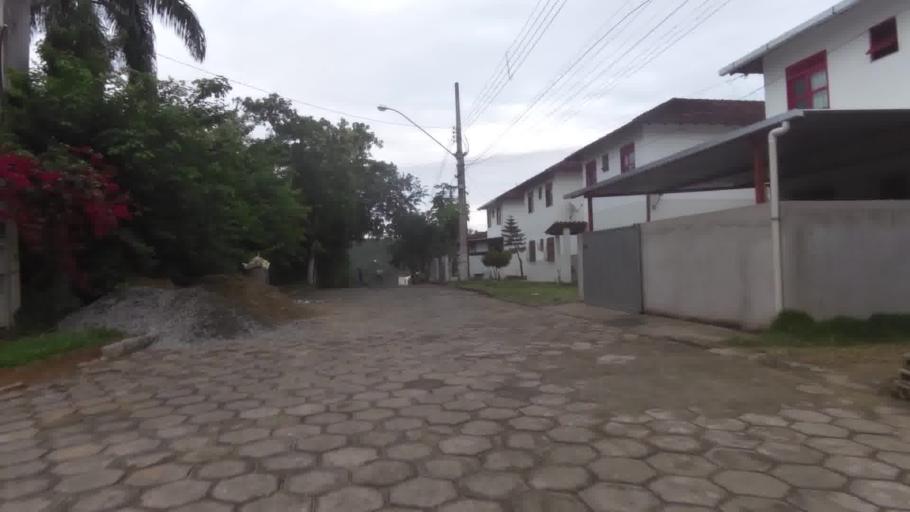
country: BR
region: Espirito Santo
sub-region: Iconha
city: Iconha
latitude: -20.7869
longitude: -40.8179
